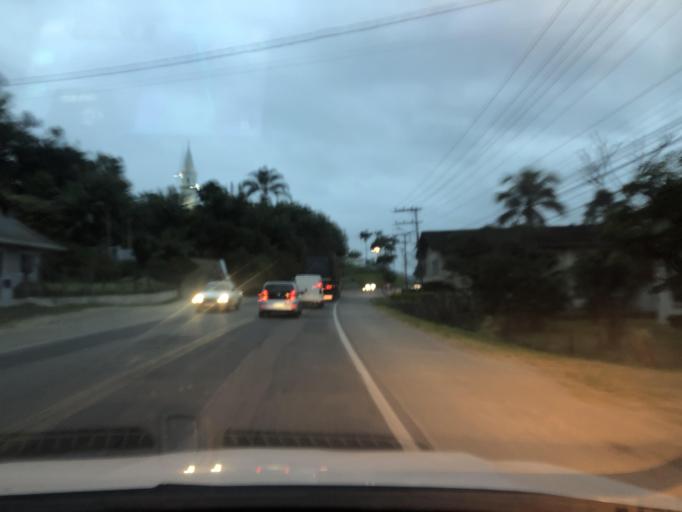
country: BR
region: Santa Catarina
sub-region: Pomerode
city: Pomerode
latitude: -26.7874
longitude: -49.0859
